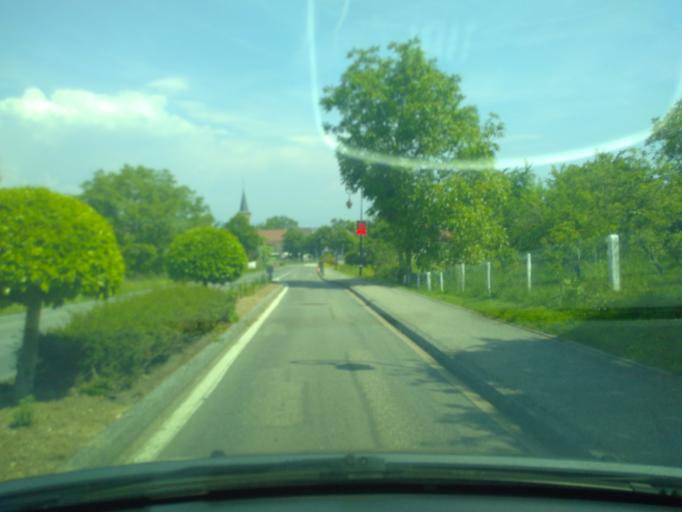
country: FR
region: Rhone-Alpes
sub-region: Departement de la Haute-Savoie
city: Archamps
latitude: 46.1331
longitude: 6.1326
